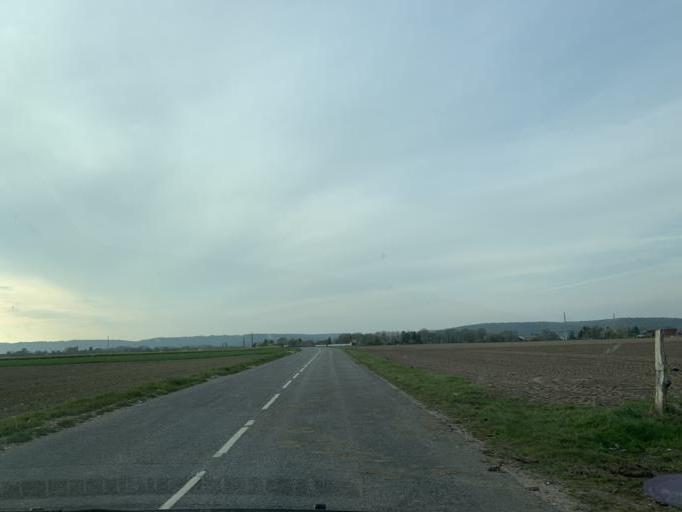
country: FR
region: Haute-Normandie
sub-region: Departement de la Seine-Maritime
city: La Mailleraye-sur-Seine
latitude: 49.4994
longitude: 0.7542
